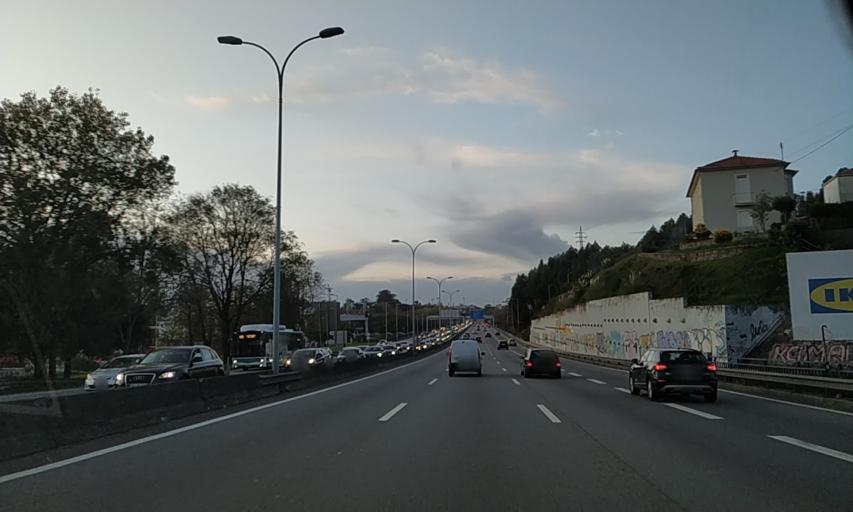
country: PT
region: Porto
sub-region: Matosinhos
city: Matosinhos
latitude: 41.1921
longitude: -8.6795
